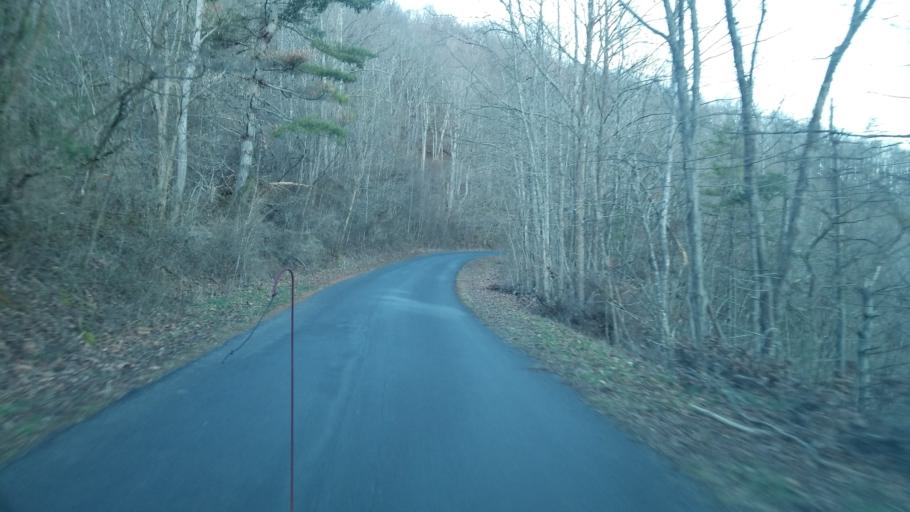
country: US
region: Virginia
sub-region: Pulaski County
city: Pulaski
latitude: 37.1644
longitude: -80.8592
